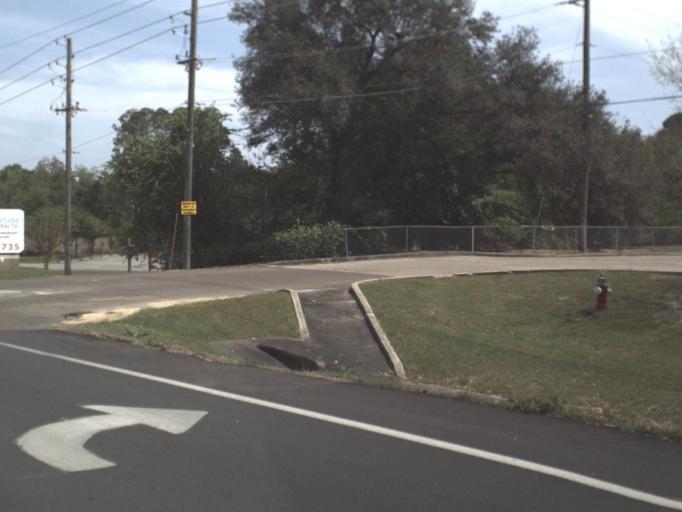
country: US
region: Florida
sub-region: Escambia County
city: Ferry Pass
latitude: 30.5324
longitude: -87.2367
